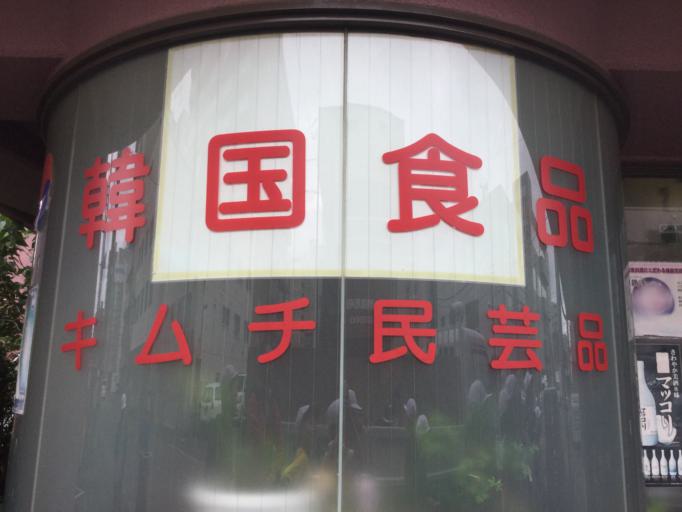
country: JP
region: Hokkaido
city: Sapporo
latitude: 43.0479
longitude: 141.3490
